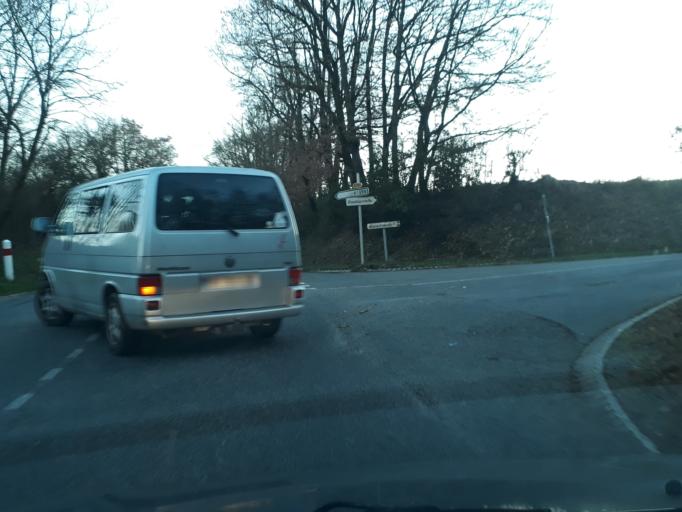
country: FR
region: Midi-Pyrenees
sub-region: Departement du Gers
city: Pujaudran
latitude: 43.5630
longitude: 1.1278
